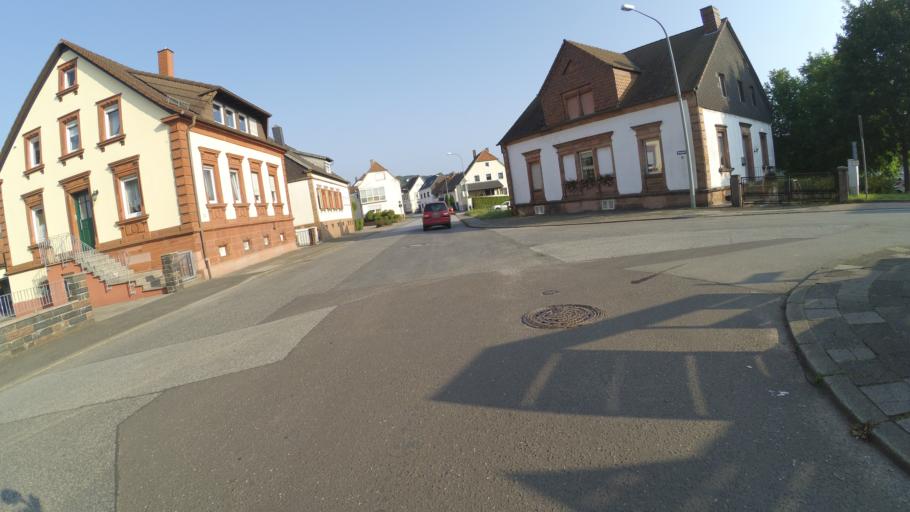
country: DE
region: Rheinland-Pfalz
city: Schonenberg-Kubelberg
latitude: 49.4066
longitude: 7.3762
